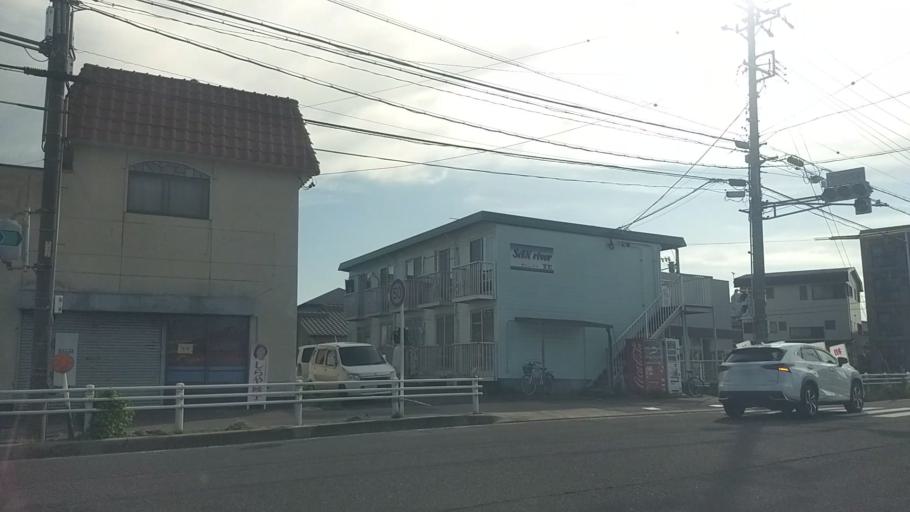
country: JP
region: Aichi
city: Anjo
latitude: 34.9483
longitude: 137.0939
